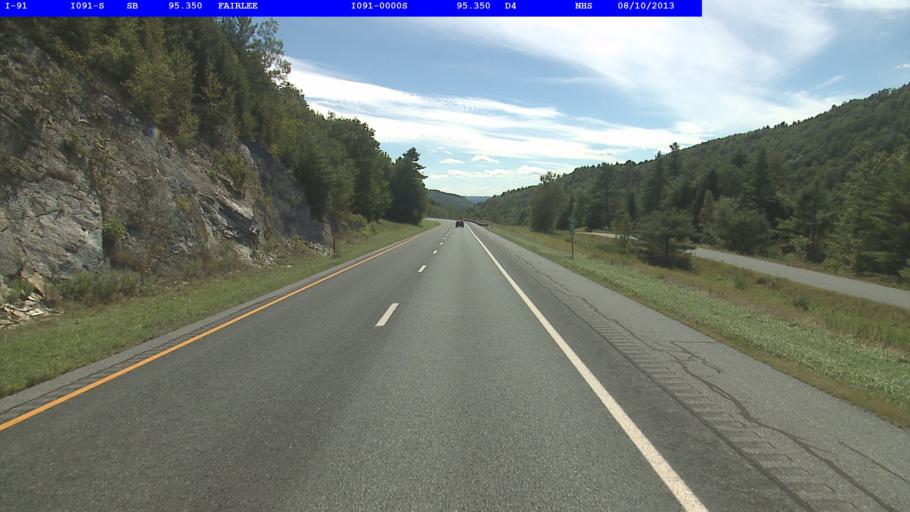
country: US
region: New Hampshire
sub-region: Grafton County
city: Orford
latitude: 43.9528
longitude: -72.1318
